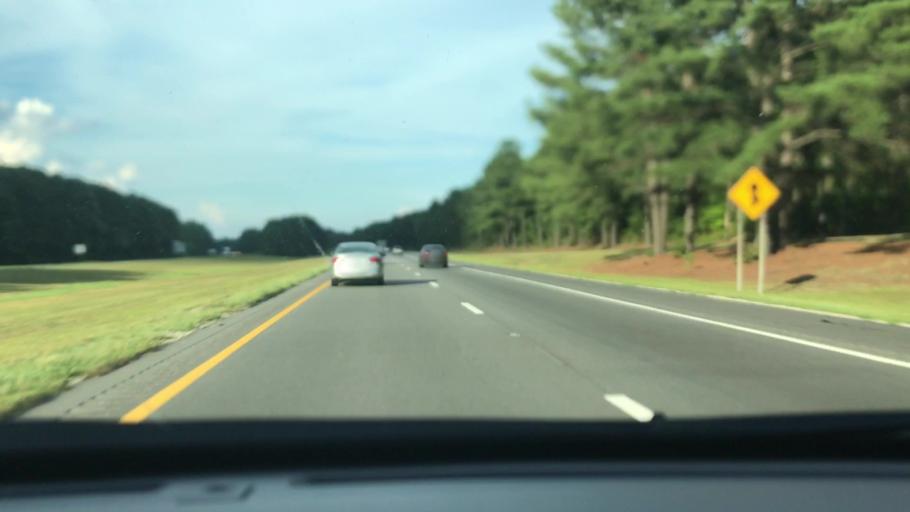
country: US
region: North Carolina
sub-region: Cumberland County
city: Hope Mills
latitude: 34.9389
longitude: -78.9214
